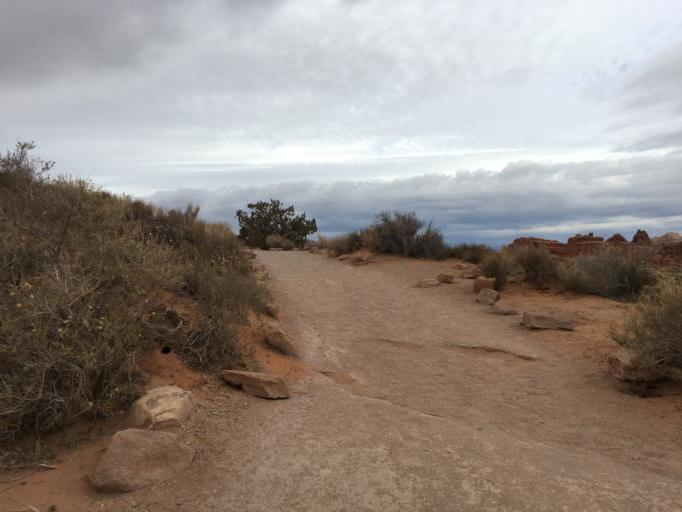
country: US
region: Utah
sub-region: Grand County
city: Moab
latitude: 38.7894
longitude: -109.6020
